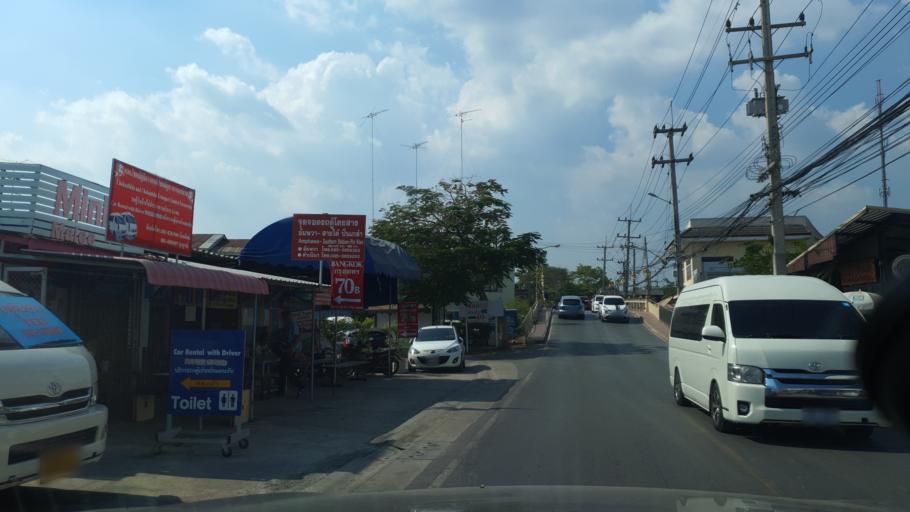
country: TH
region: Samut Songkhram
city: Amphawa
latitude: 13.4256
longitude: 99.9560
